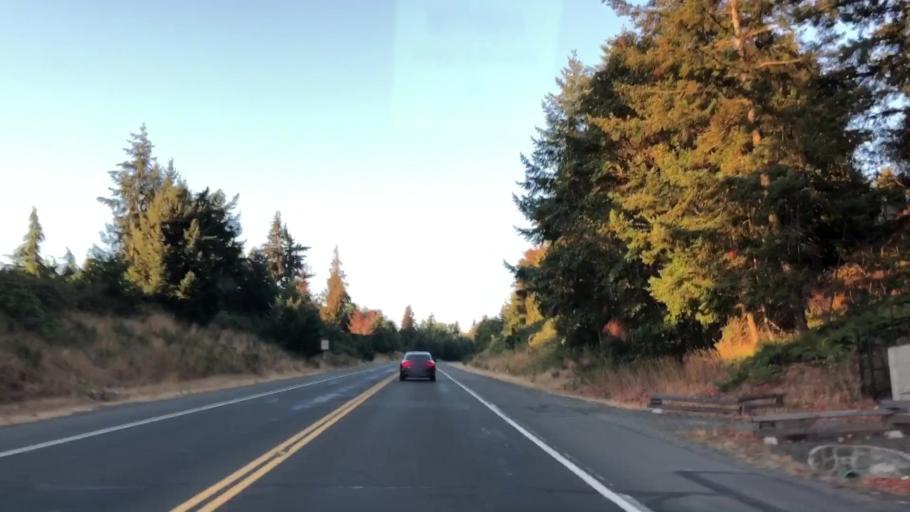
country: CA
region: British Columbia
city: Colwood
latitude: 48.4249
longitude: -123.5023
